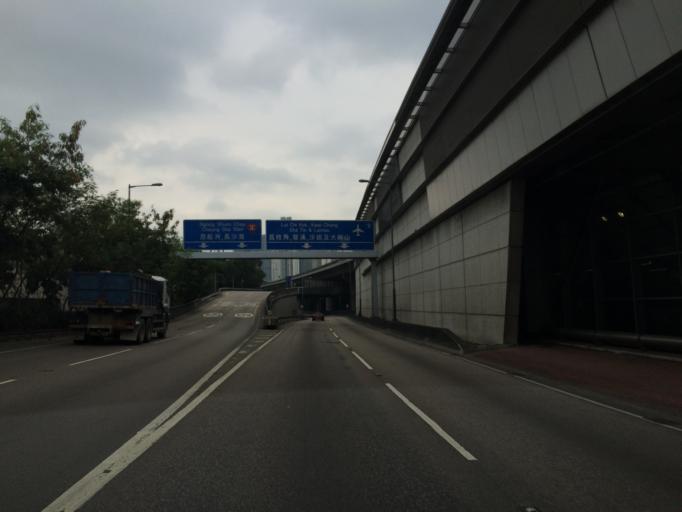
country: HK
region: Sham Shui Po
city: Sham Shui Po
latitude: 22.3264
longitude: 114.1529
